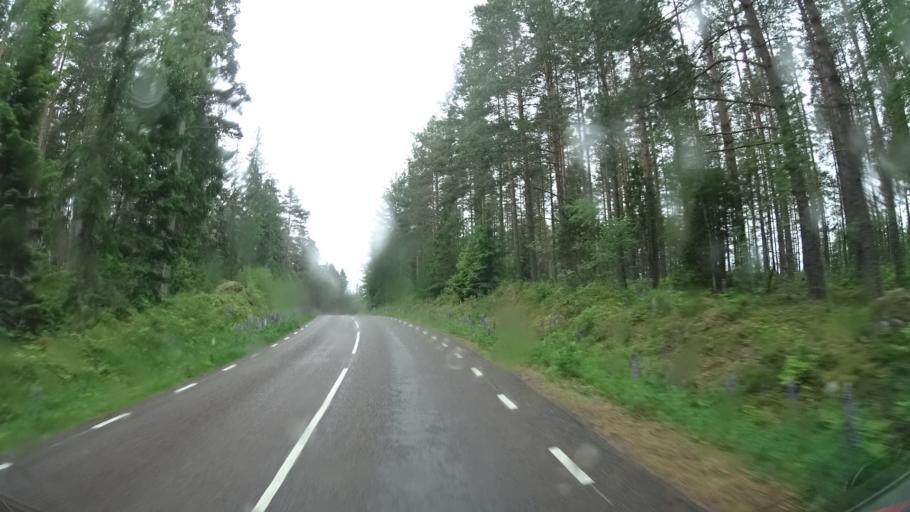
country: SE
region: Joenkoeping
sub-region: Eksjo Kommun
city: Mariannelund
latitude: 57.6535
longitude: 15.6004
